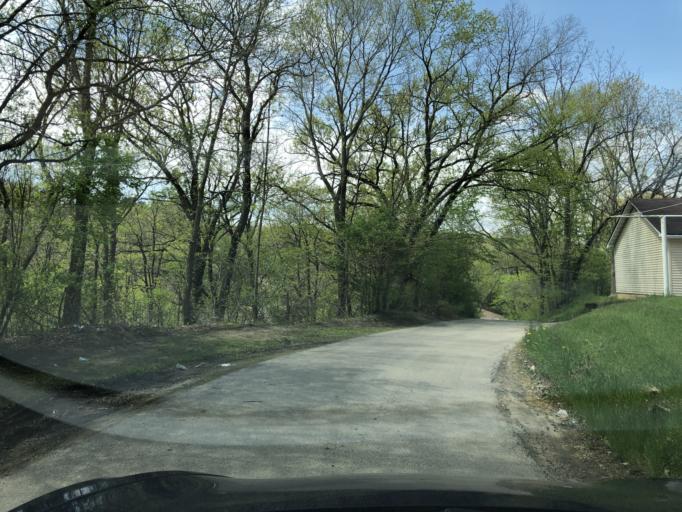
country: US
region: Iowa
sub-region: Dubuque County
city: Dubuque
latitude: 42.4813
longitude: -90.6704
